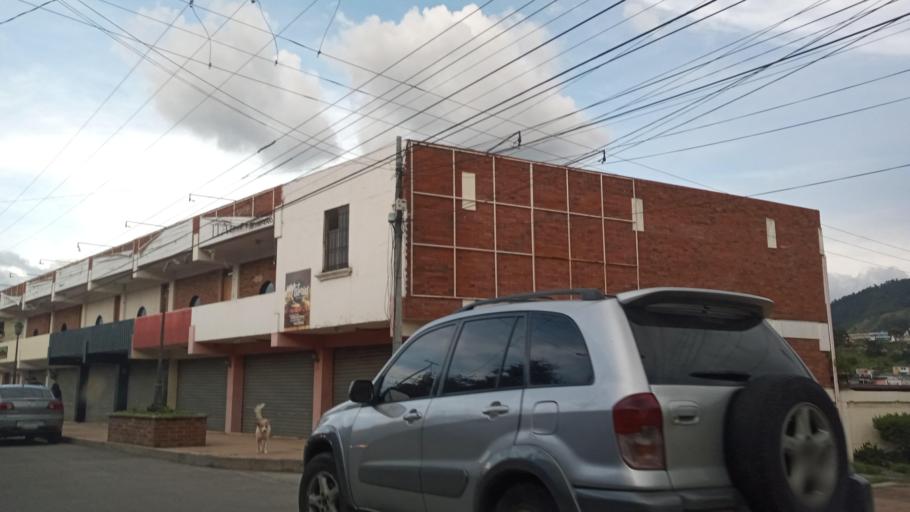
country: GT
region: Quetzaltenango
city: Quetzaltenango
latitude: 14.8377
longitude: -91.5120
